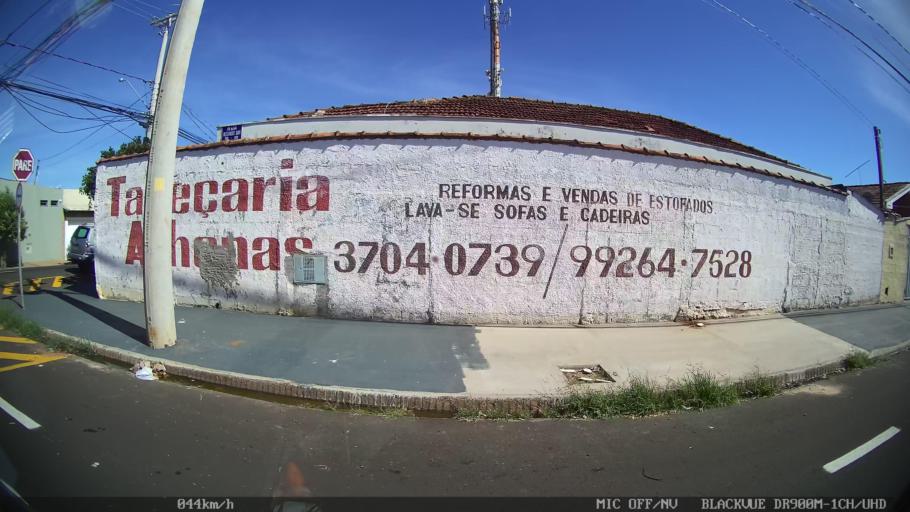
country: BR
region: Sao Paulo
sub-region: Franca
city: Franca
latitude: -20.5453
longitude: -47.3890
